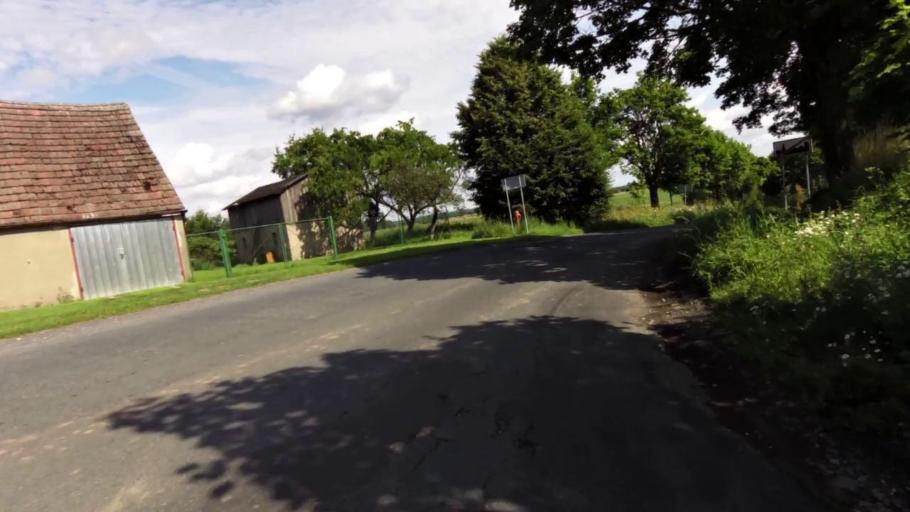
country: PL
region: West Pomeranian Voivodeship
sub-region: Powiat stargardzki
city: Dobrzany
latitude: 53.4140
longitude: 15.4173
